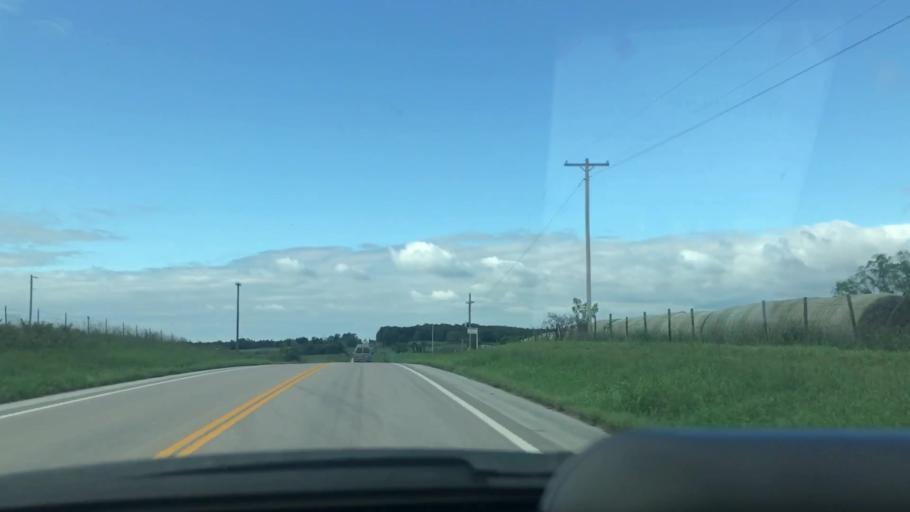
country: US
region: Missouri
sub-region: Hickory County
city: Hermitage
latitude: 37.9546
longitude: -93.2073
